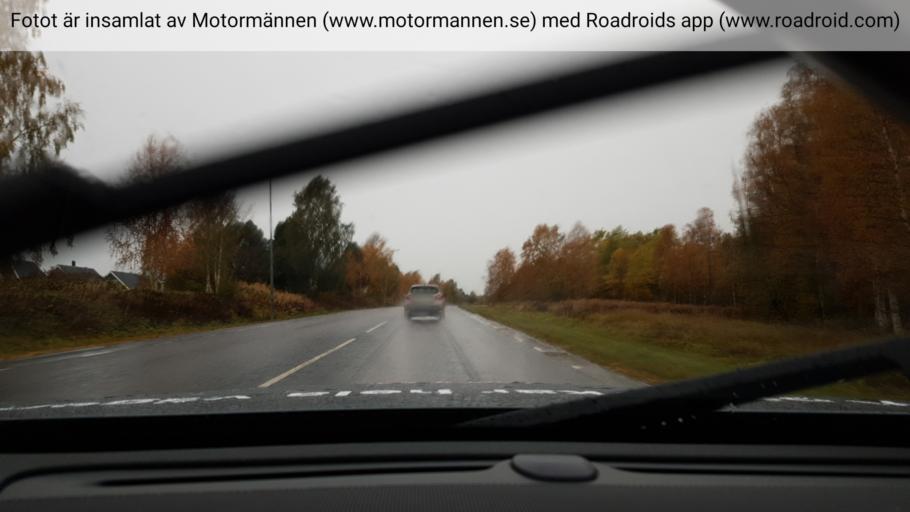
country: SE
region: Norrbotten
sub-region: Lulea Kommun
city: Sodra Sunderbyn
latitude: 65.6557
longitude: 21.9671
